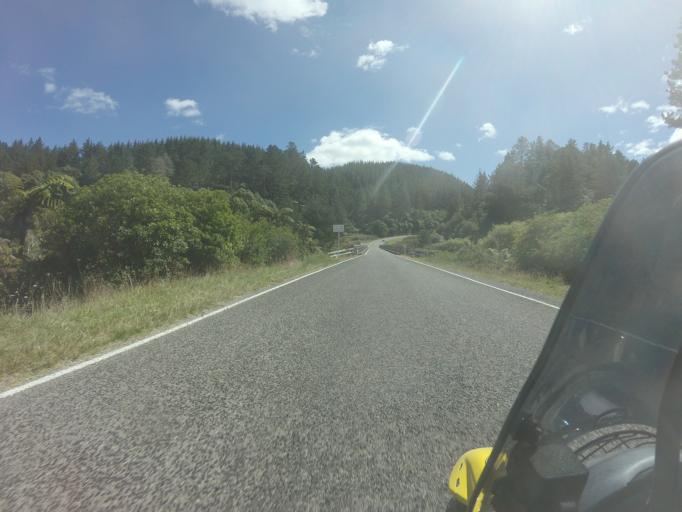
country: NZ
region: Bay of Plenty
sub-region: Kawerau District
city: Kawerau
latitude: -38.1775
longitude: 176.8305
